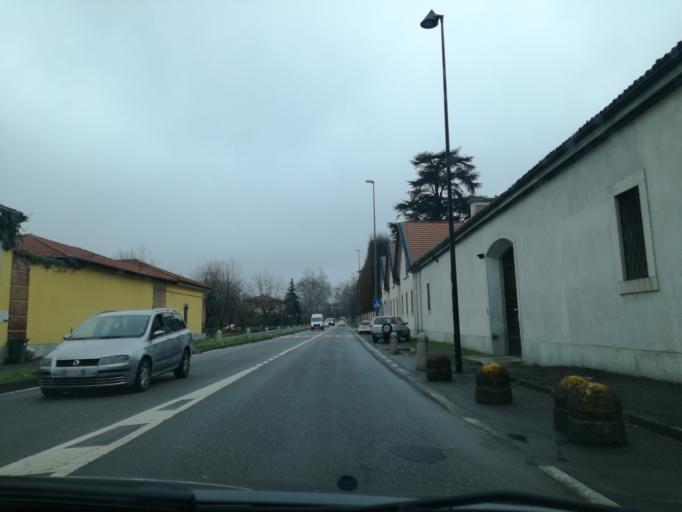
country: IT
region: Lombardy
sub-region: Provincia di Lecco
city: Verderio Superiore
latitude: 45.6699
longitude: 9.4384
